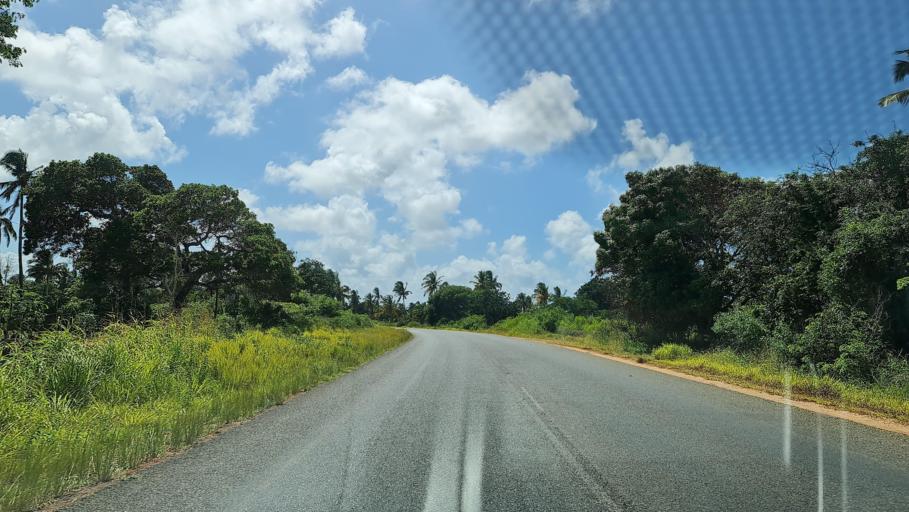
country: MZ
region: Inhambane
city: Maxixe
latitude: -24.5400
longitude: 34.9321
